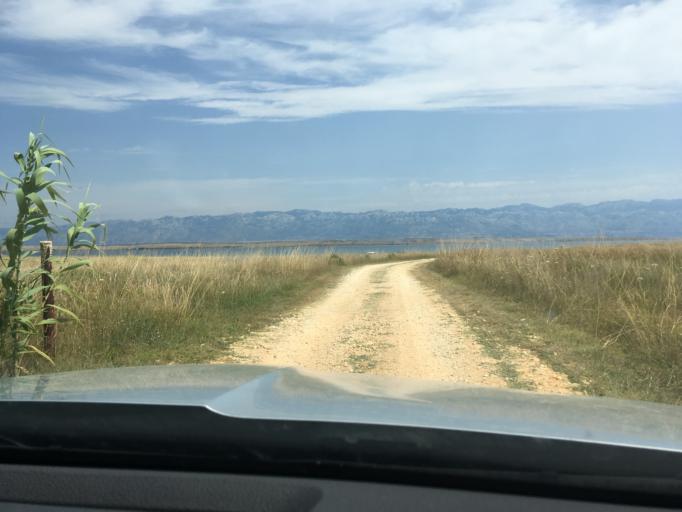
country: HR
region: Zadarska
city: Privlaka
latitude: 44.2674
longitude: 15.1517
